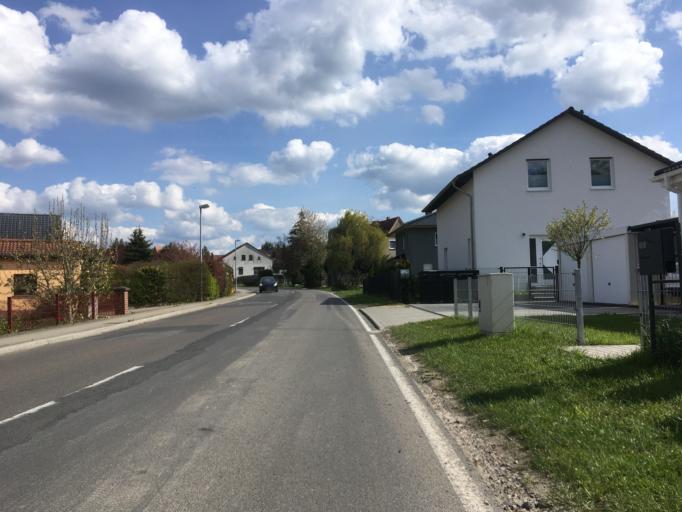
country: DE
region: Brandenburg
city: Altlandsberg
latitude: 52.5984
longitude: 13.6888
